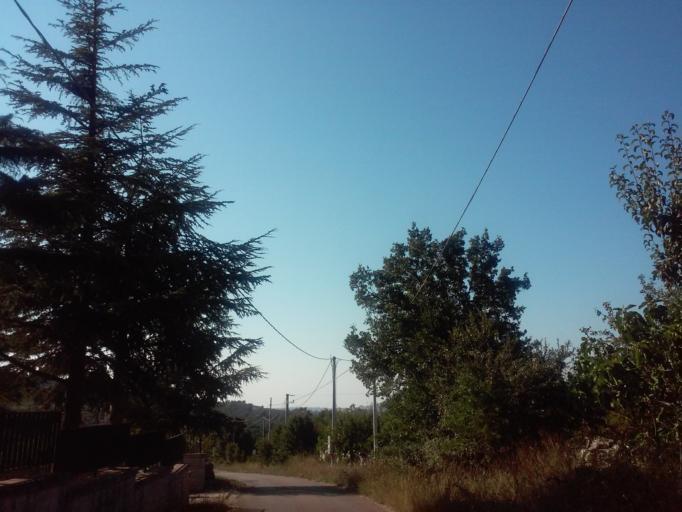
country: IT
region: Apulia
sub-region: Provincia di Bari
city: Noci
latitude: 40.8163
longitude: 17.1598
